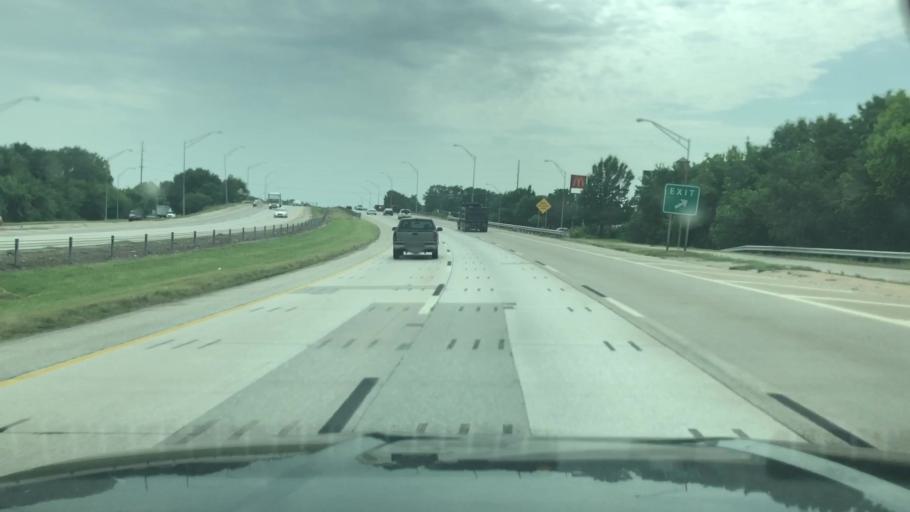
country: US
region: Oklahoma
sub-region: Tulsa County
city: Tulsa
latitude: 36.1570
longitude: -96.0167
